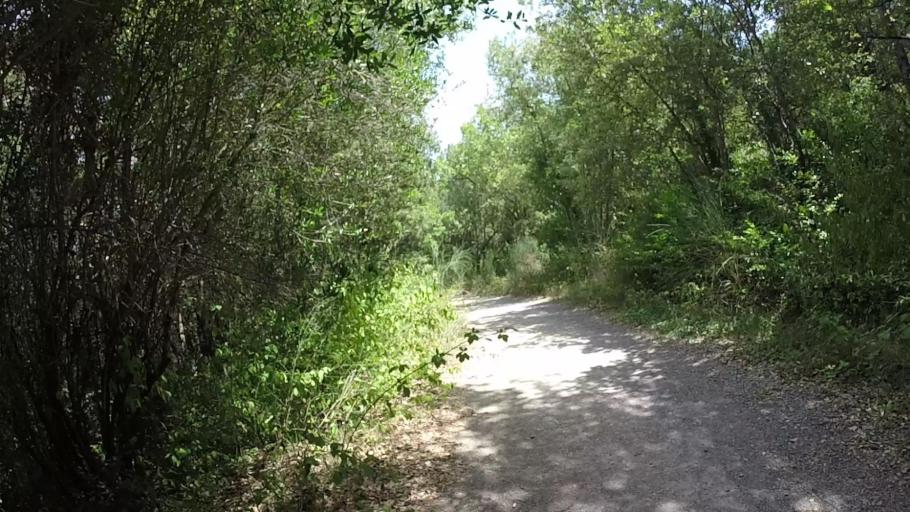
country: FR
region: Provence-Alpes-Cote d'Azur
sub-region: Departement des Alpes-Maritimes
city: Mougins
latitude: 43.6182
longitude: 7.0201
